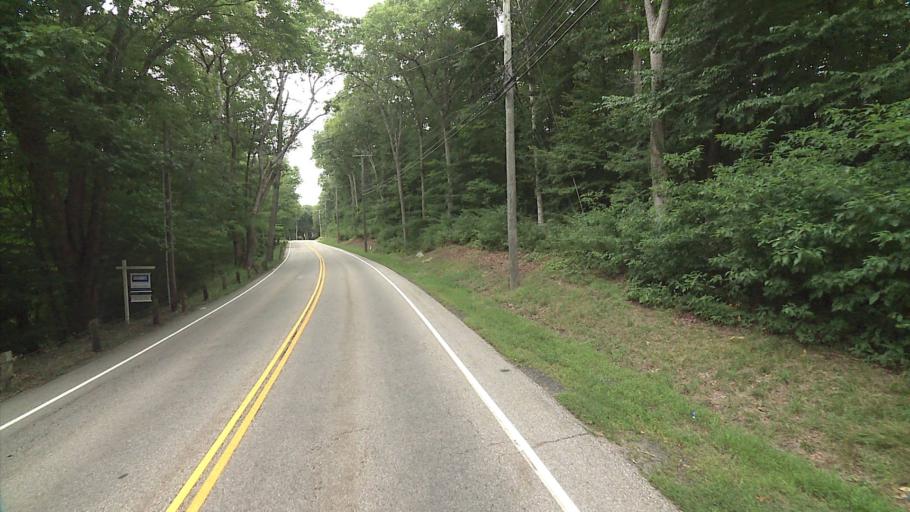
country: US
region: Connecticut
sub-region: Middlesex County
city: Essex Village
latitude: 41.4059
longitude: -72.3400
